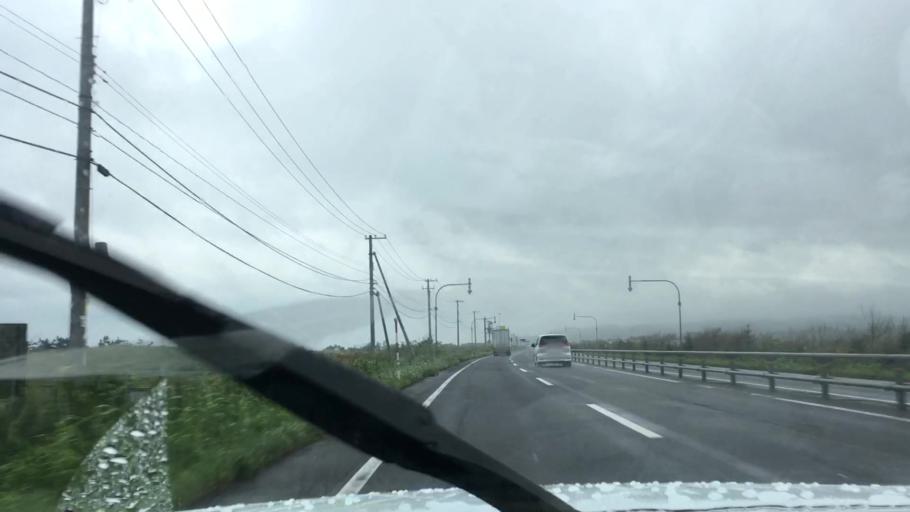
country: JP
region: Hokkaido
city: Niseko Town
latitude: 42.4021
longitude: 140.3038
